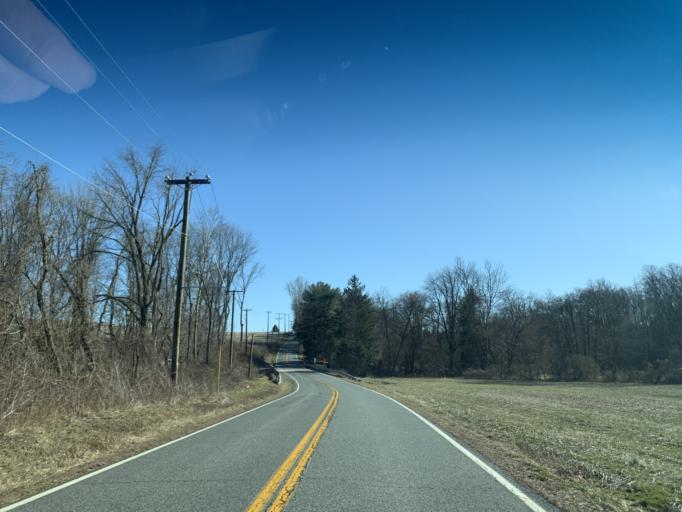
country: US
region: Maryland
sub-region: Cecil County
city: Rising Sun
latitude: 39.6591
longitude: -76.1036
